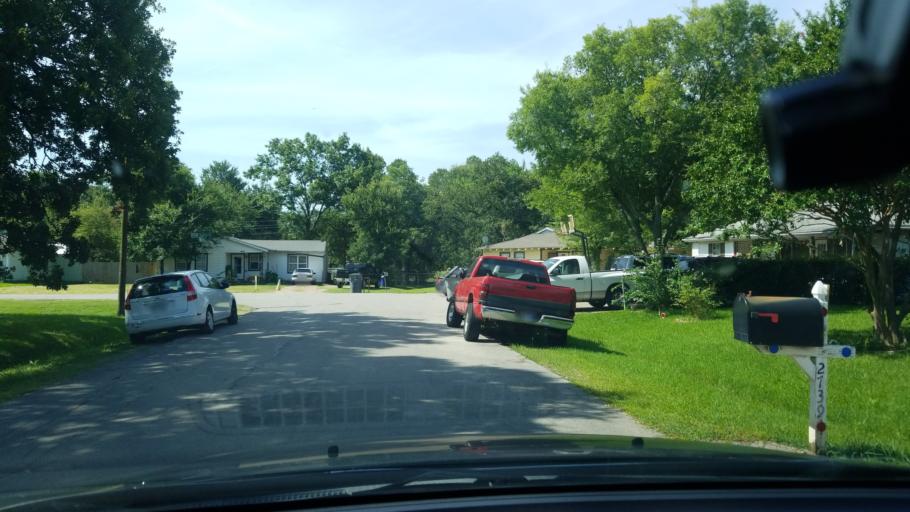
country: US
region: Texas
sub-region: Dallas County
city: Balch Springs
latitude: 32.7313
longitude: -96.6264
